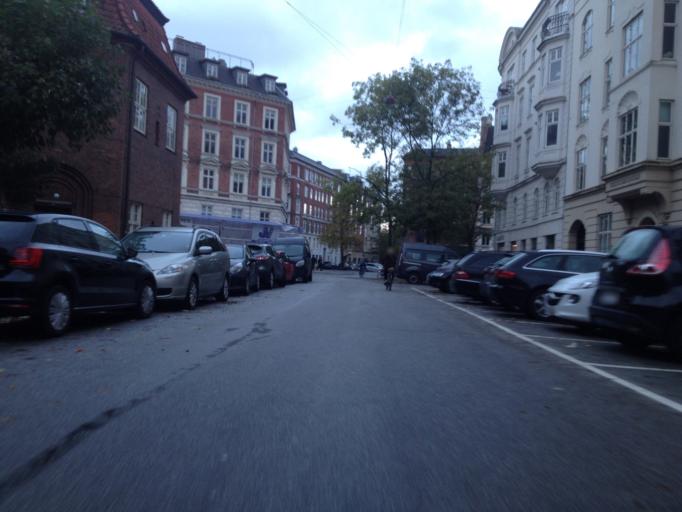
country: DK
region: Capital Region
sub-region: Kobenhavn
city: Copenhagen
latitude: 55.7024
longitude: 12.5807
